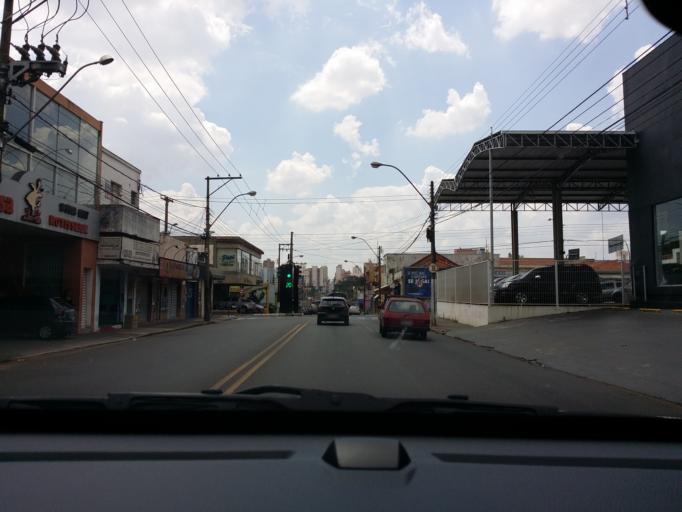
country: BR
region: Sao Paulo
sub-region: Sao Carlos
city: Sao Carlos
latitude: -22.0274
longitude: -47.8905
